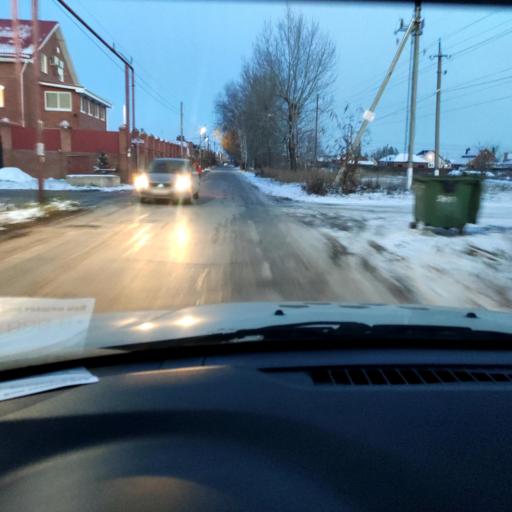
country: RU
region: Samara
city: Tol'yatti
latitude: 53.5605
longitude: 49.3829
